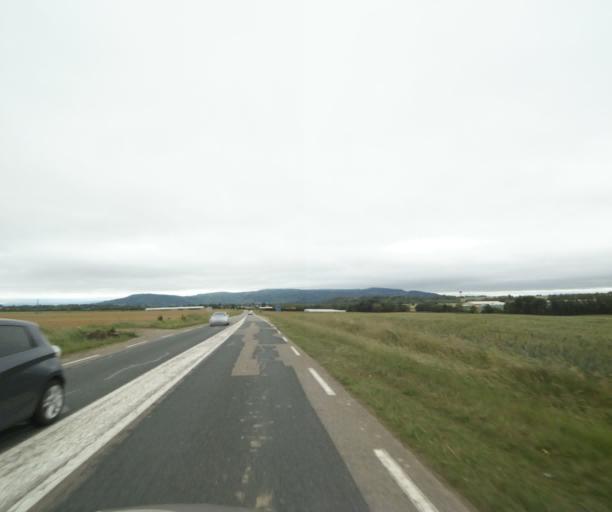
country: FR
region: Rhone-Alpes
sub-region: Departement du Rhone
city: Cailloux-sur-Fontaines
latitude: 45.8632
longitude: 4.8972
